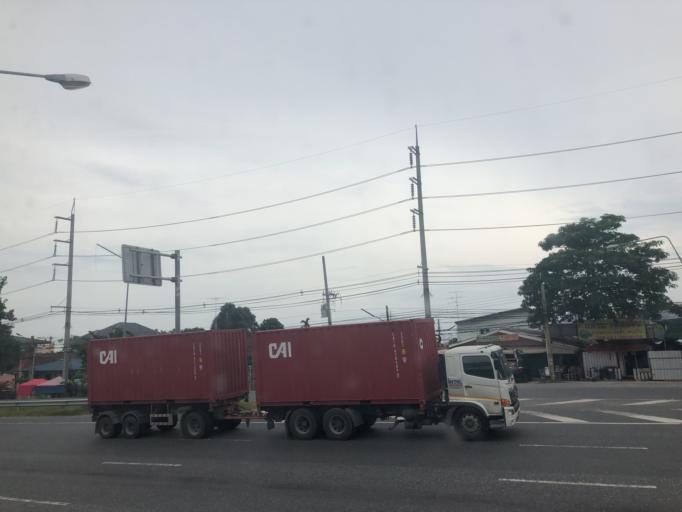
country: TH
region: Chon Buri
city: Bang Lamung
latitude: 13.0723
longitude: 100.9221
